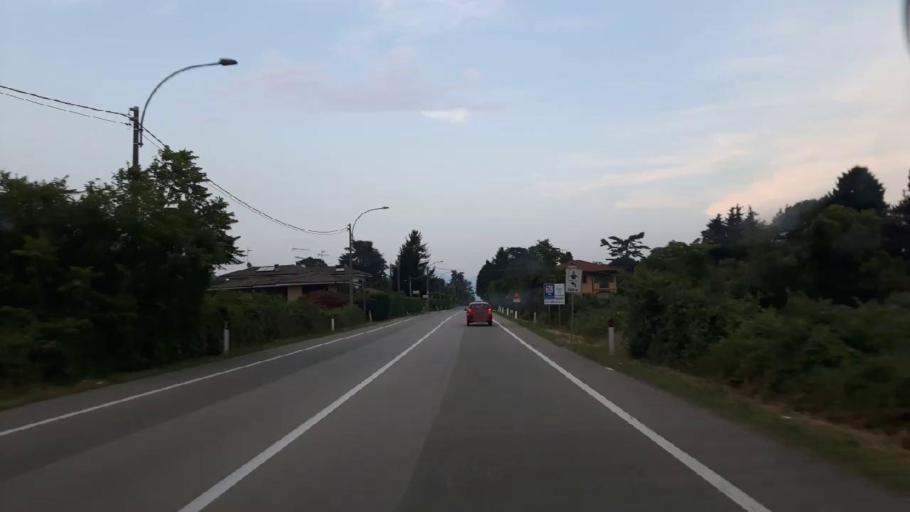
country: IT
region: Piedmont
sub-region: Provincia di Novara
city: Lesa
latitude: 45.8207
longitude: 8.5550
